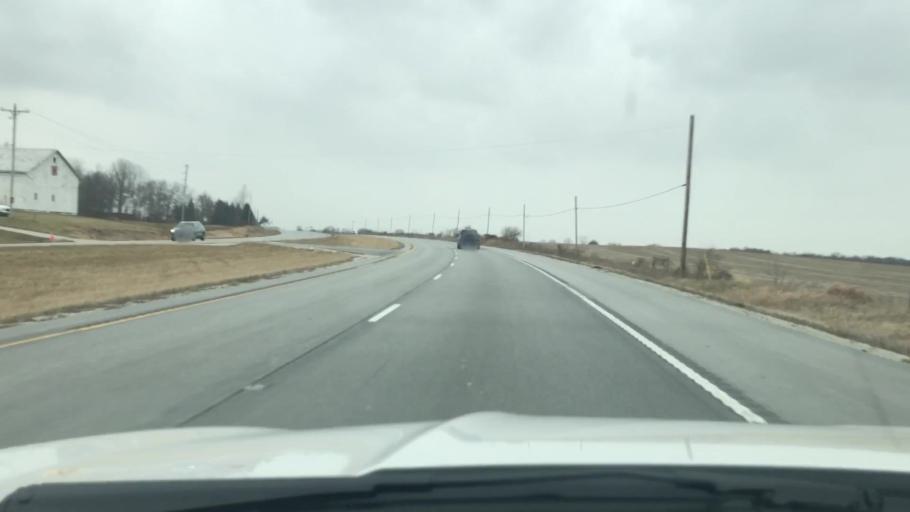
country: US
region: Indiana
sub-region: Miami County
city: Peru
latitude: 40.8474
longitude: -86.1279
